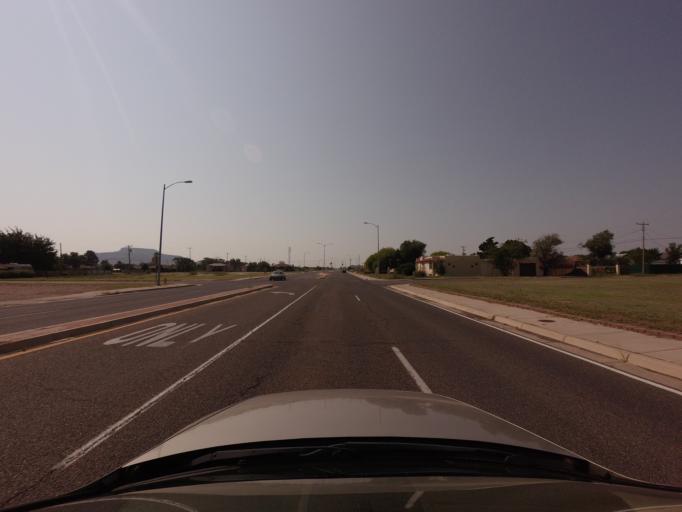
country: US
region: New Mexico
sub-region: Quay County
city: Tucumcari
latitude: 35.1632
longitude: -103.7250
